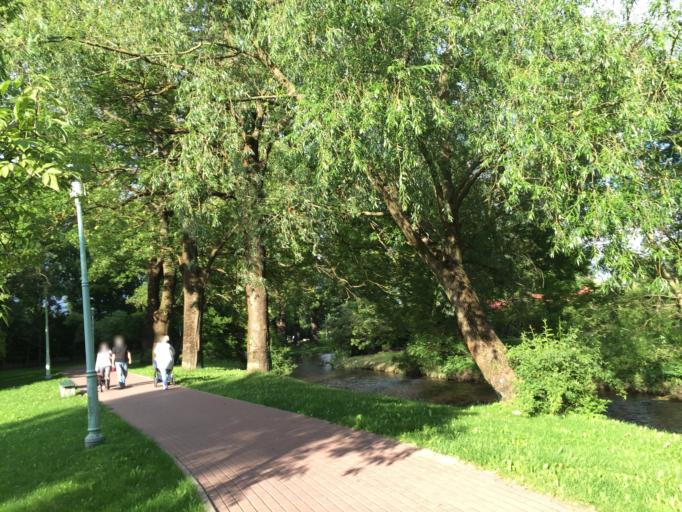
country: PL
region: Podlasie
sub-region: Suwalki
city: Suwalki
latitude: 54.0936
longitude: 22.9329
